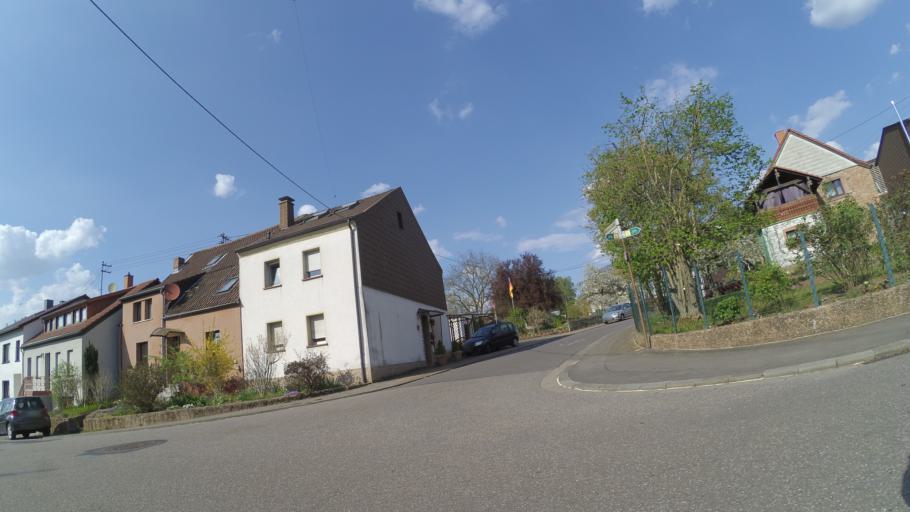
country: DE
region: Saarland
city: Riegelsberg
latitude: 49.3102
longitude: 6.9428
